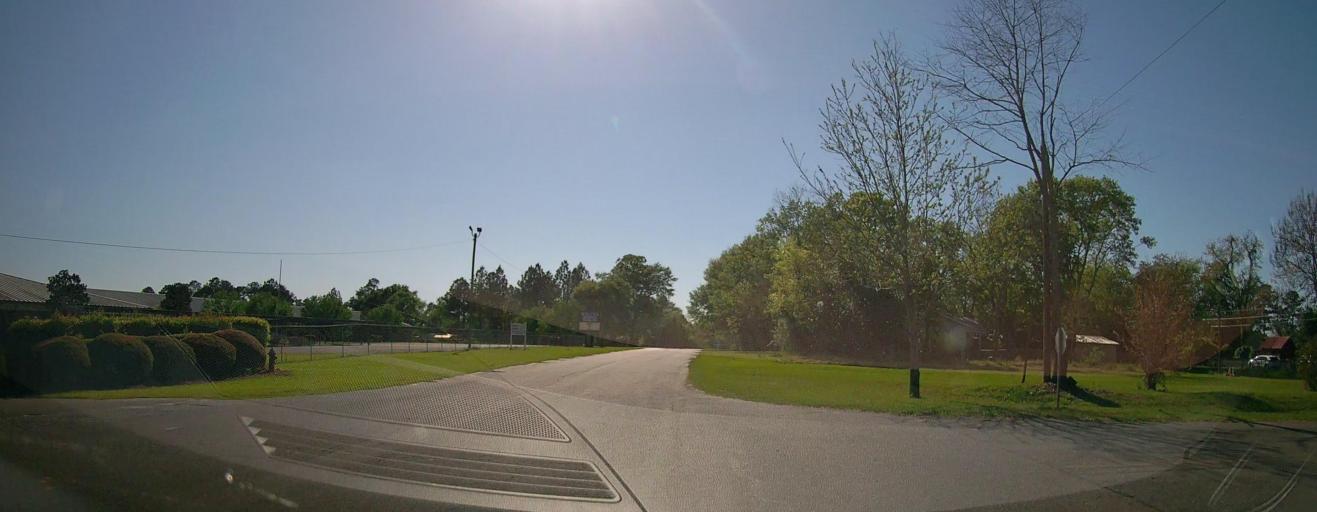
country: US
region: Georgia
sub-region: Wilcox County
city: Rochelle
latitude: 31.9440
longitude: -83.4530
